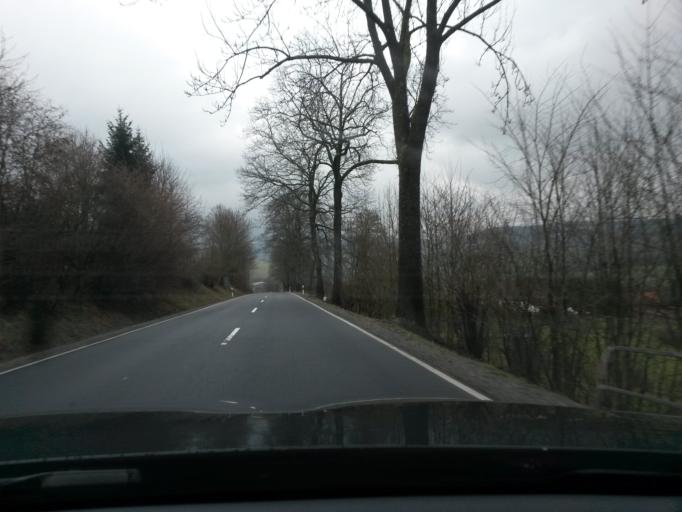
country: DE
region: Thuringia
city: Birx
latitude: 50.4873
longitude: 9.9896
